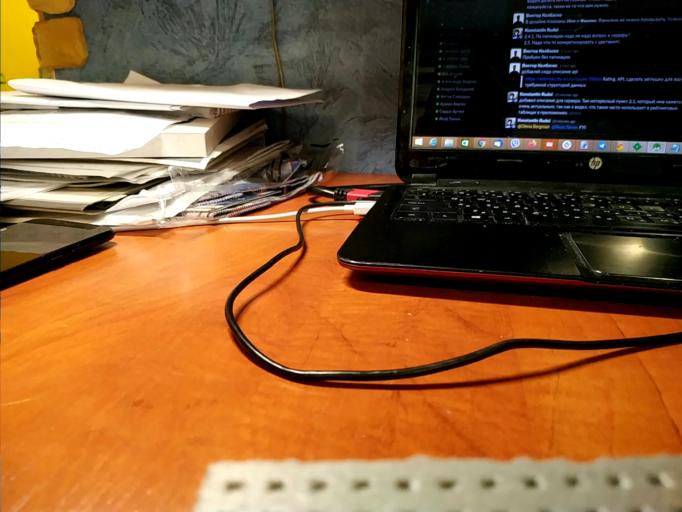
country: RU
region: Tverskaya
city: Spirovo
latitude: 57.4514
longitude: 34.9182
